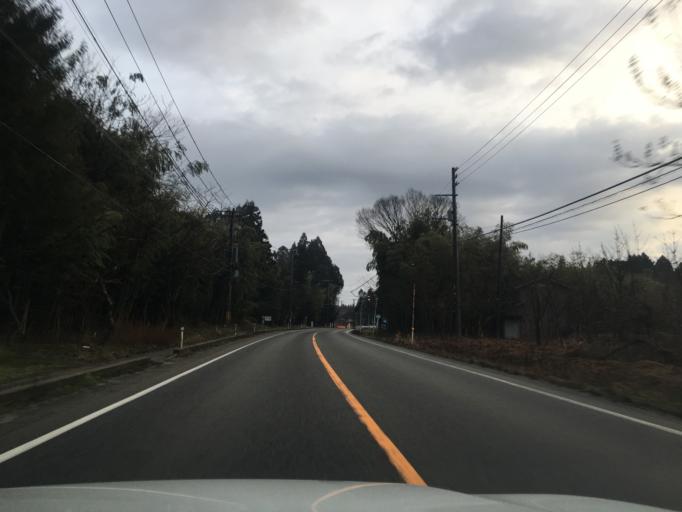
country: JP
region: Niigata
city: Murakami
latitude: 38.2924
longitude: 139.5286
